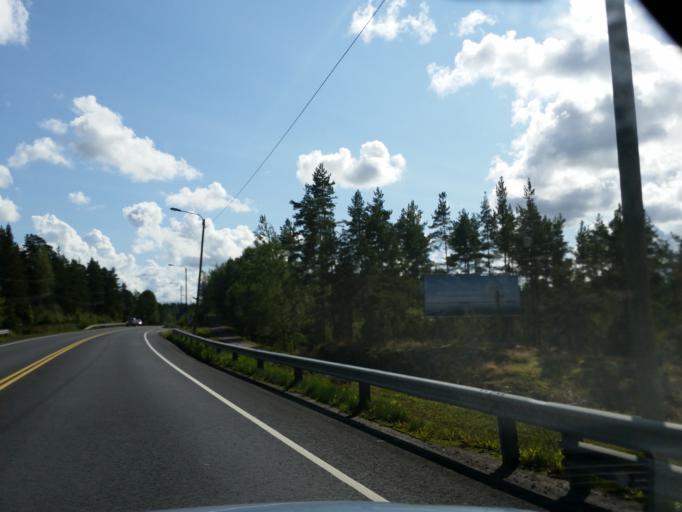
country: FI
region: Varsinais-Suomi
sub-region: Turku
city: Kaarina
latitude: 60.3524
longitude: 22.3598
